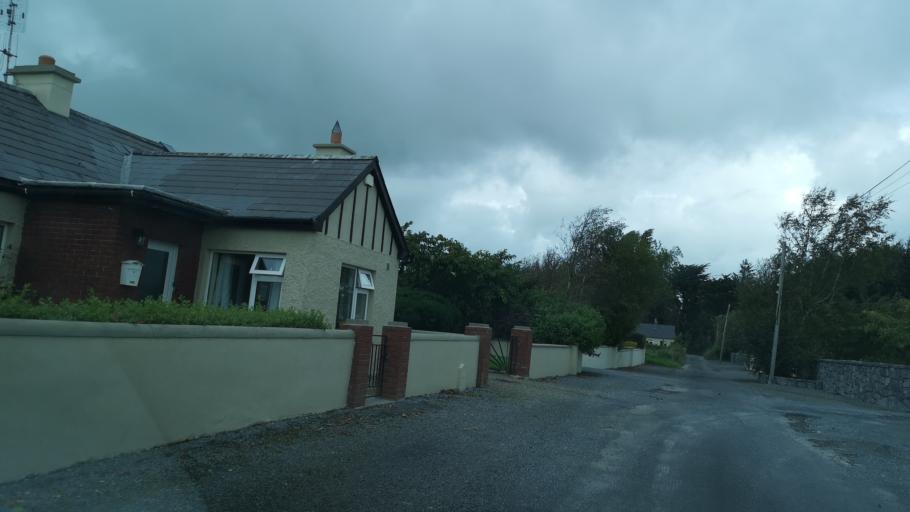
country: IE
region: Connaught
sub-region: County Galway
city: Athenry
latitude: 53.3061
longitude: -8.6986
